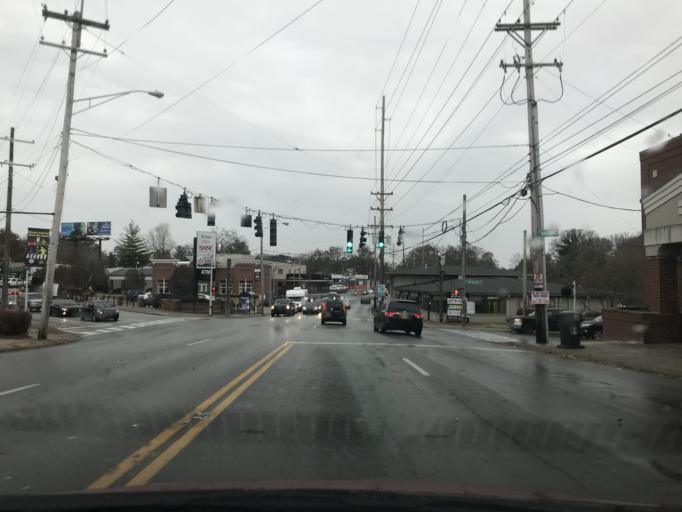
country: US
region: Kentucky
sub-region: Jefferson County
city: West Buechel
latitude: 38.2232
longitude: -85.6851
